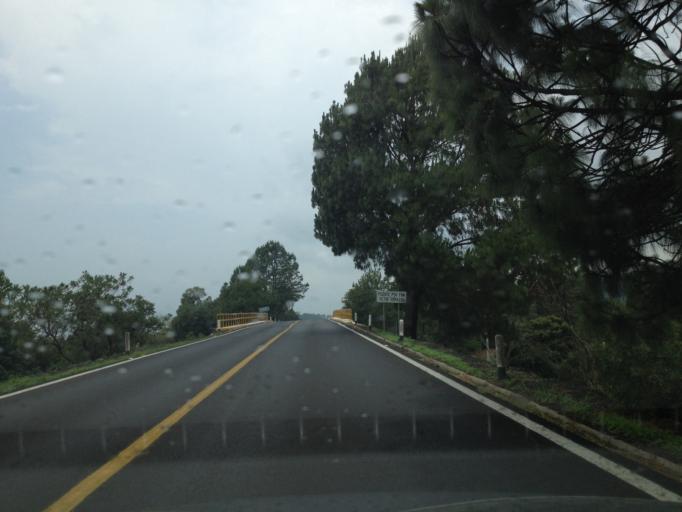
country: MX
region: Michoacan
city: Tingambato
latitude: 19.5055
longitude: -101.8621
